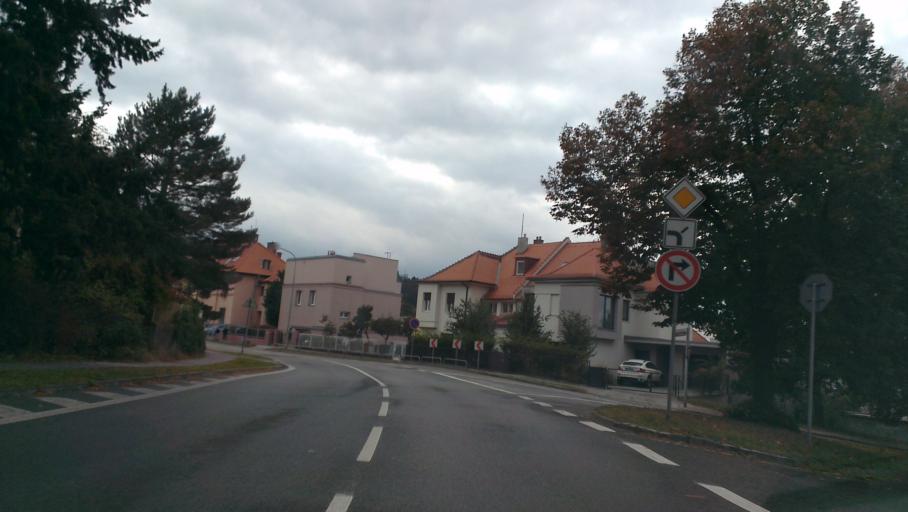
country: CZ
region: South Moravian
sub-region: Mesto Brno
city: Brno
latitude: 49.2076
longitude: 16.5829
